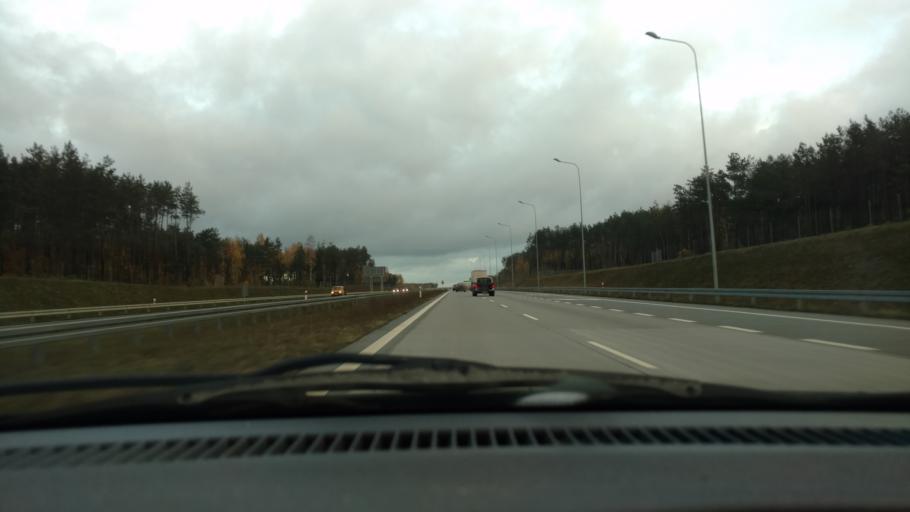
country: PL
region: Lodz Voivodeship
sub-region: Powiat lodzki wschodni
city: Tuszyn
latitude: 51.6523
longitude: 19.5781
